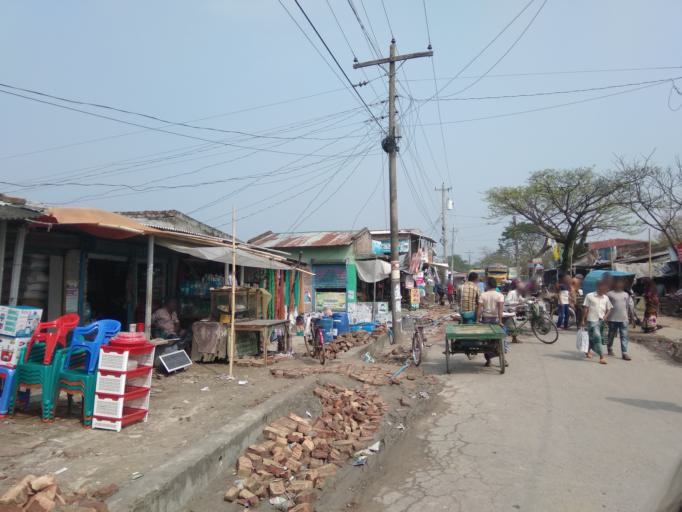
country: IN
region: West Bengal
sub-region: North 24 Parganas
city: Gosaba
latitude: 22.2699
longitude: 89.1959
